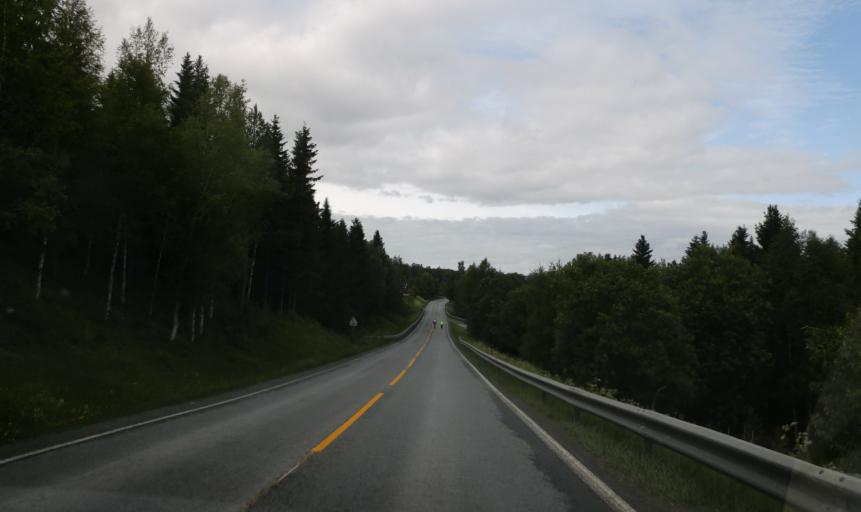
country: NO
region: Nord-Trondelag
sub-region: Stjordal
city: Stjordalshalsen
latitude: 63.4004
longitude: 10.9479
